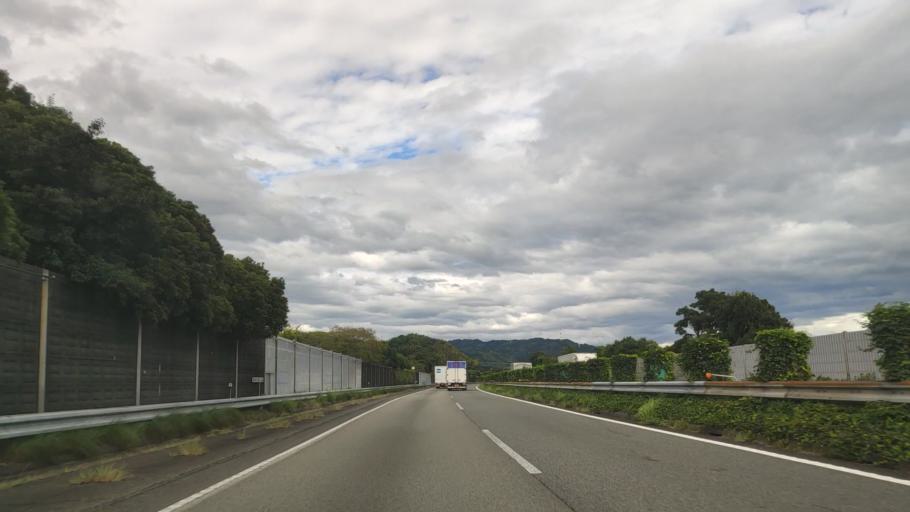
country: JP
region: Shizuoka
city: Shizuoka-shi
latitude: 35.0342
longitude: 138.4576
